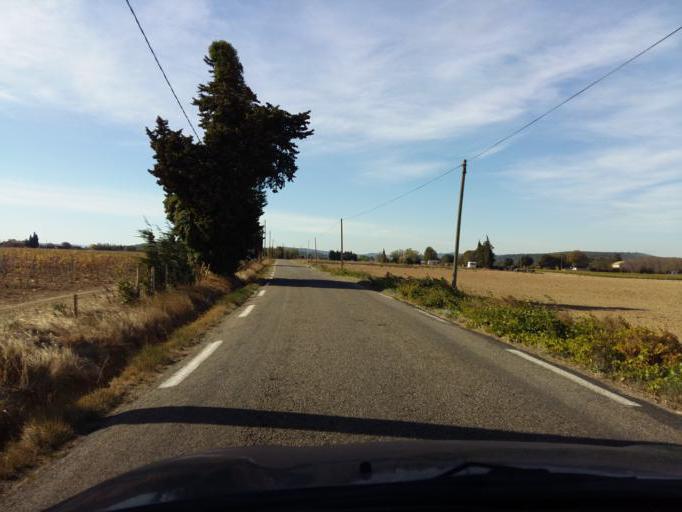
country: FR
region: Provence-Alpes-Cote d'Azur
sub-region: Departement du Vaucluse
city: Uchaux
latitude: 44.1865
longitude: 4.8105
